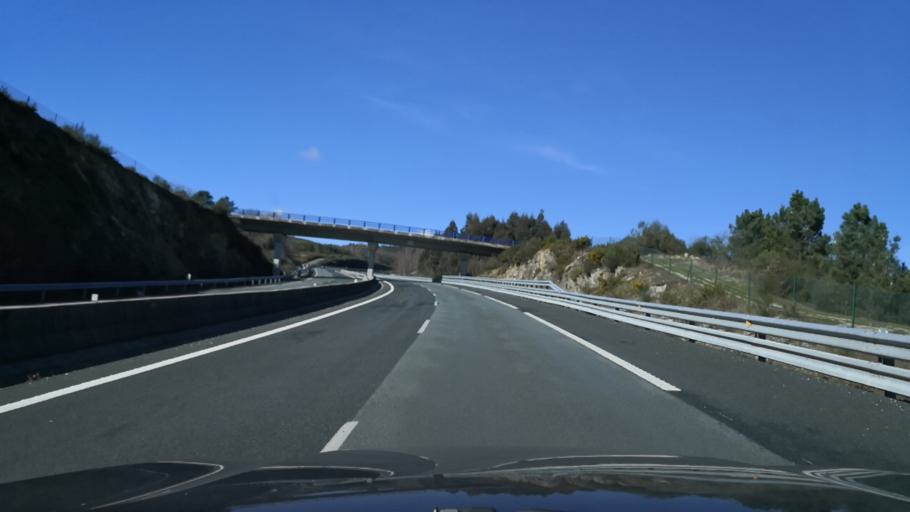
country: ES
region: Galicia
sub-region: Provincia de Ourense
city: Pinor
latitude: 42.5377
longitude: -8.0156
